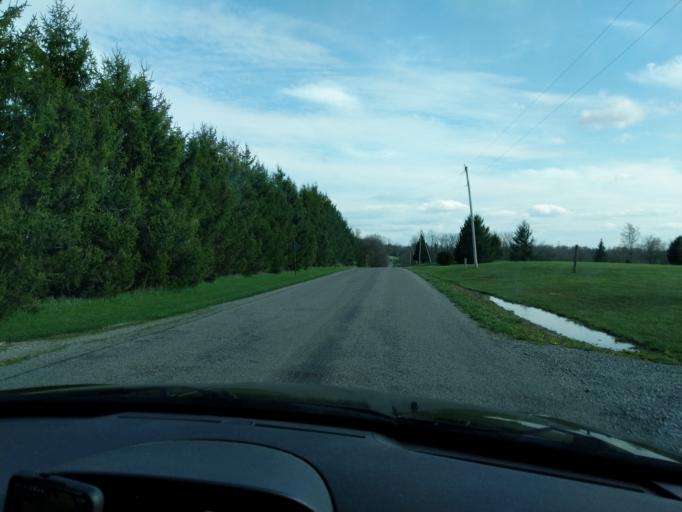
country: US
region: Ohio
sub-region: Champaign County
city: North Lewisburg
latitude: 40.1905
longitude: -83.6457
